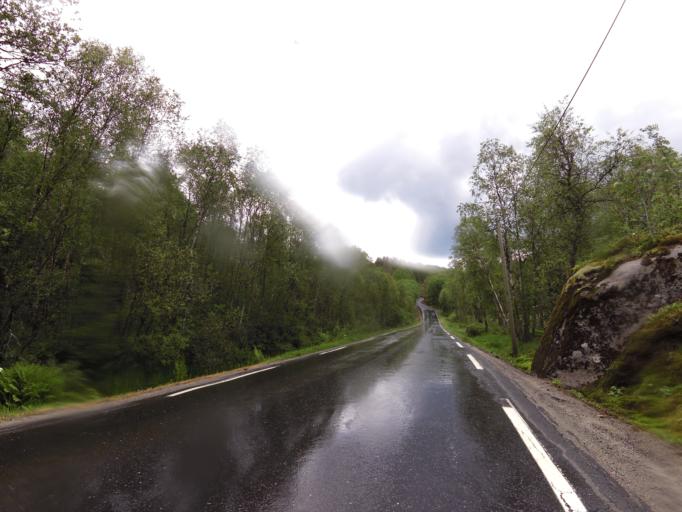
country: NO
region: Vest-Agder
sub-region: Lyngdal
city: Lyngdal
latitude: 58.1093
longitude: 7.0893
